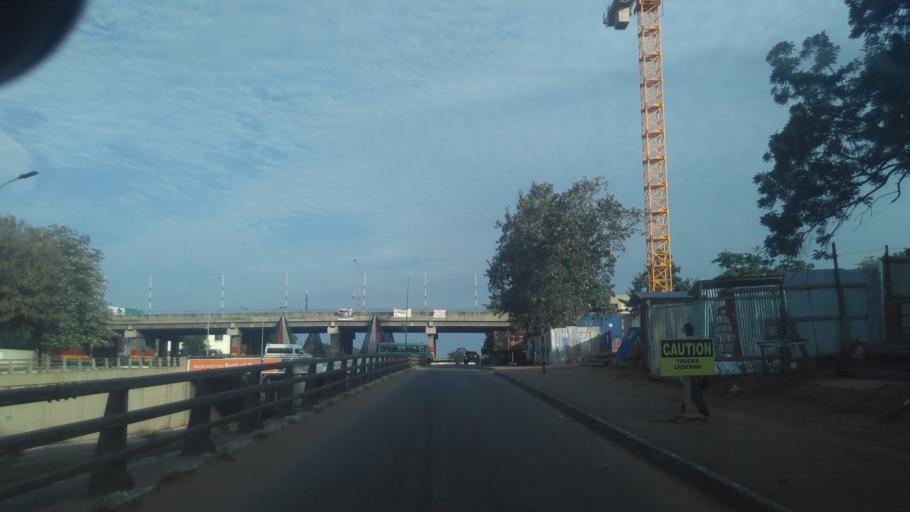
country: GH
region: Greater Accra
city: Accra
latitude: 5.5725
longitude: -0.1914
